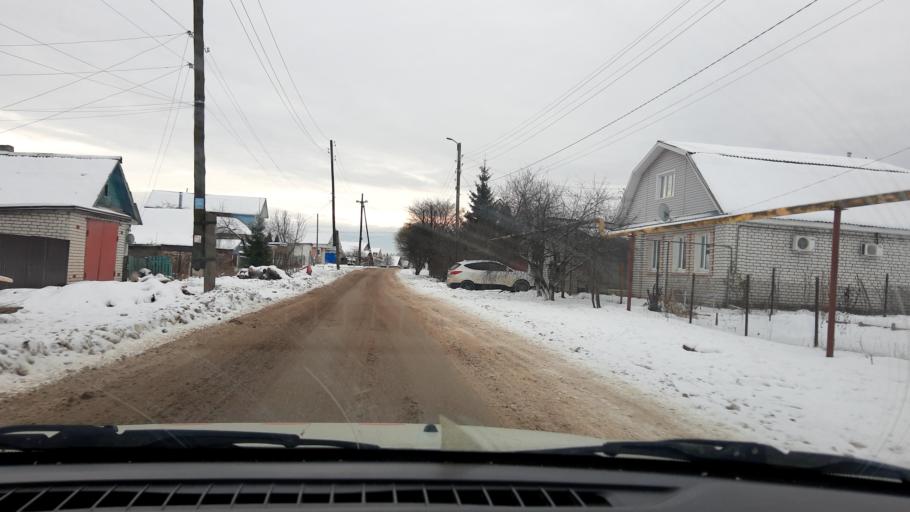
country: RU
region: Nizjnij Novgorod
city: Gorodets
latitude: 56.6618
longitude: 43.4799
